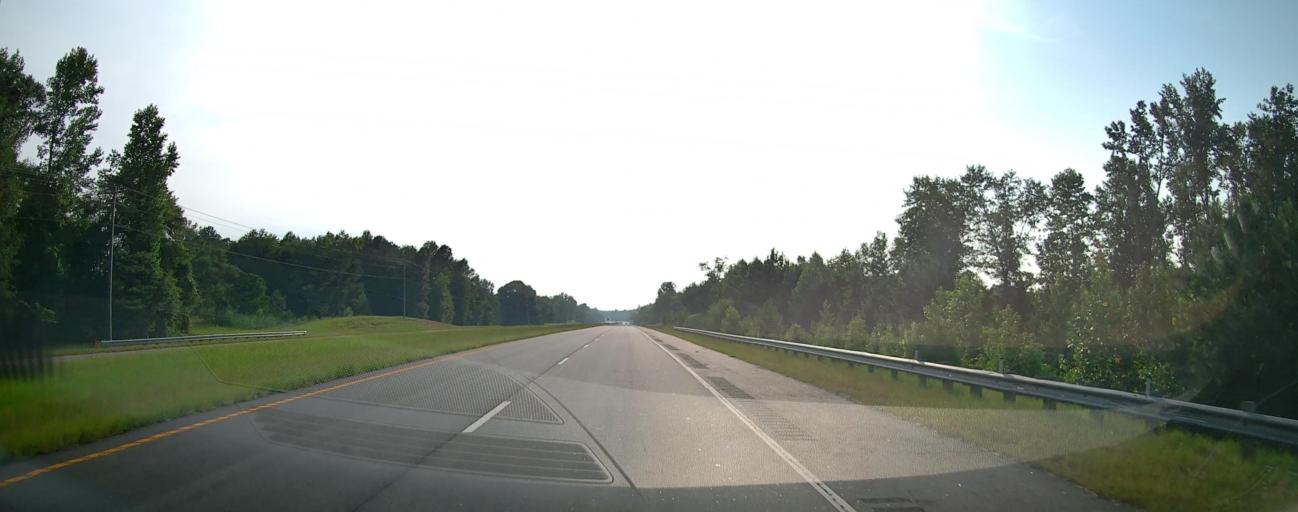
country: US
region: Georgia
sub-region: Talbot County
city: Talbotton
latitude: 32.5752
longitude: -84.5785
